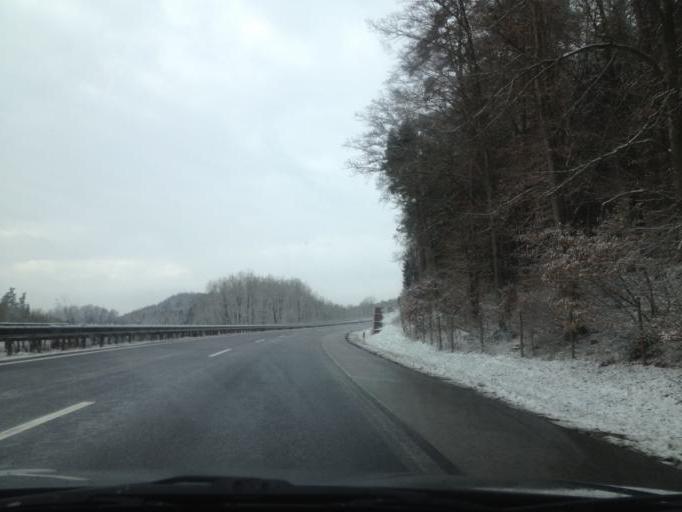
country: DE
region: Rheinland-Pfalz
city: Rodalben
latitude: 49.2078
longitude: 7.6379
